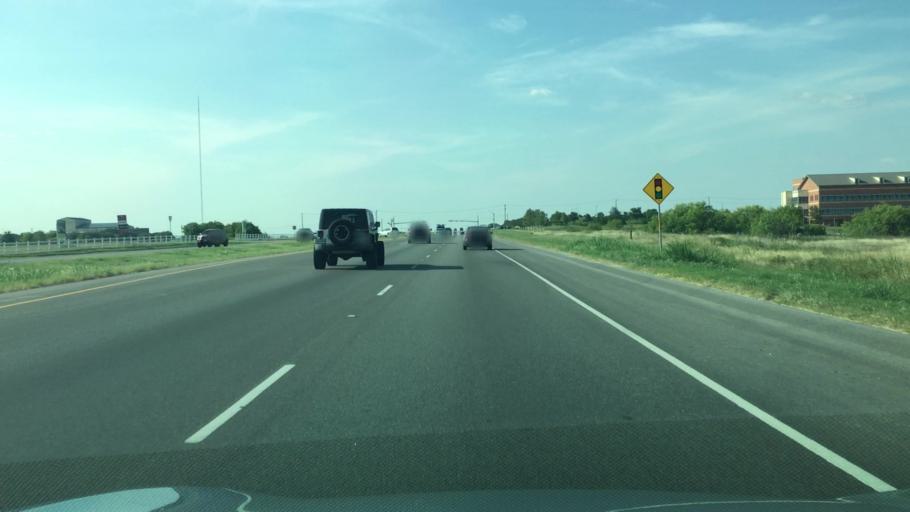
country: US
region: Texas
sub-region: Hays County
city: Kyle
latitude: 30.0234
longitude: -97.8722
